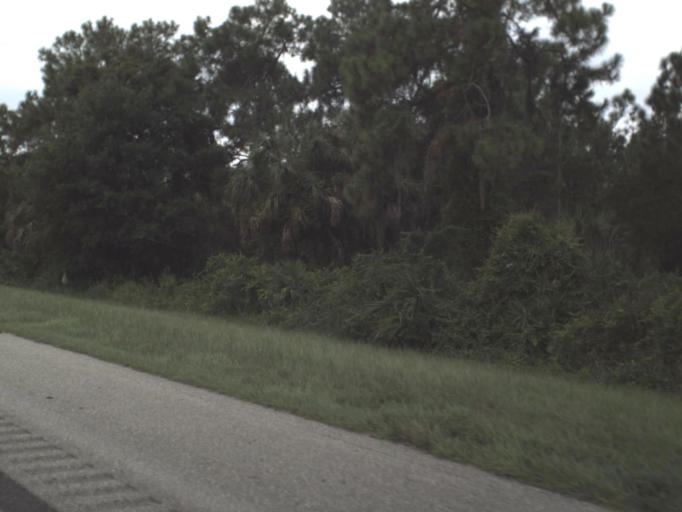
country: US
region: Florida
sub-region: Sarasota County
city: Vamo
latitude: 27.2329
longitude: -82.4529
